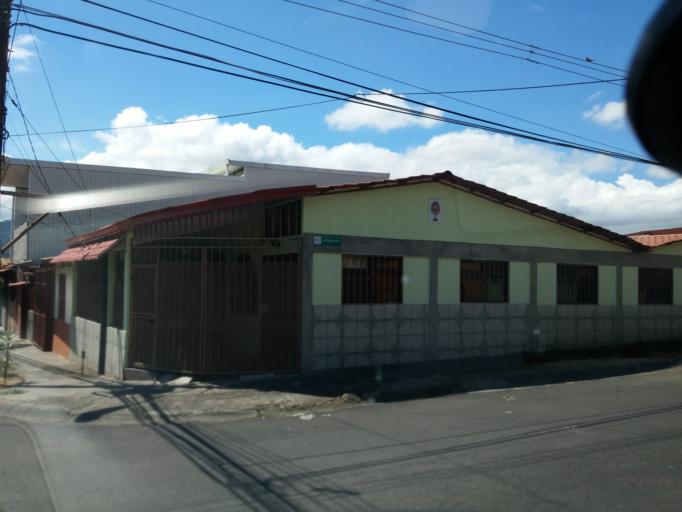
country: CR
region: San Jose
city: San Jose
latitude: 9.9158
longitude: -84.0823
